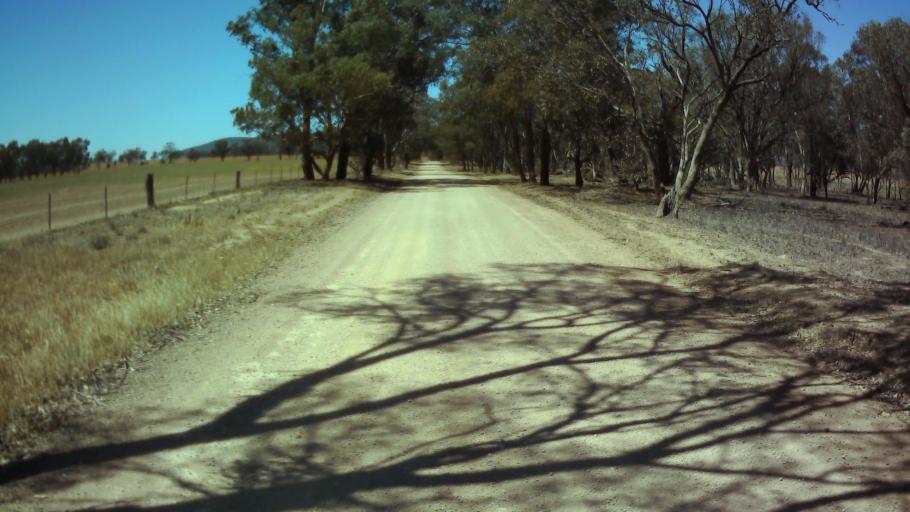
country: AU
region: New South Wales
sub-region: Weddin
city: Grenfell
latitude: -33.9253
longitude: 148.0783
